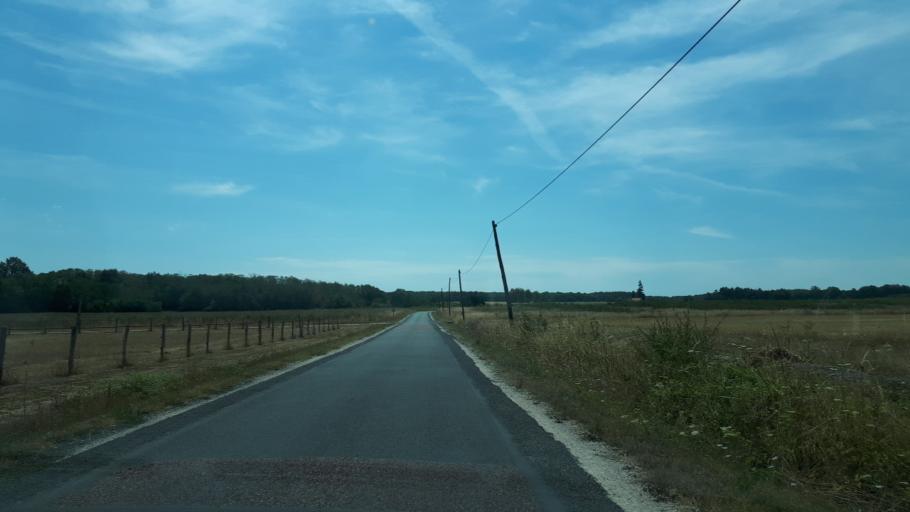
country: FR
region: Centre
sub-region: Departement du Loir-et-Cher
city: Chitenay
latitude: 47.4352
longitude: 1.3548
